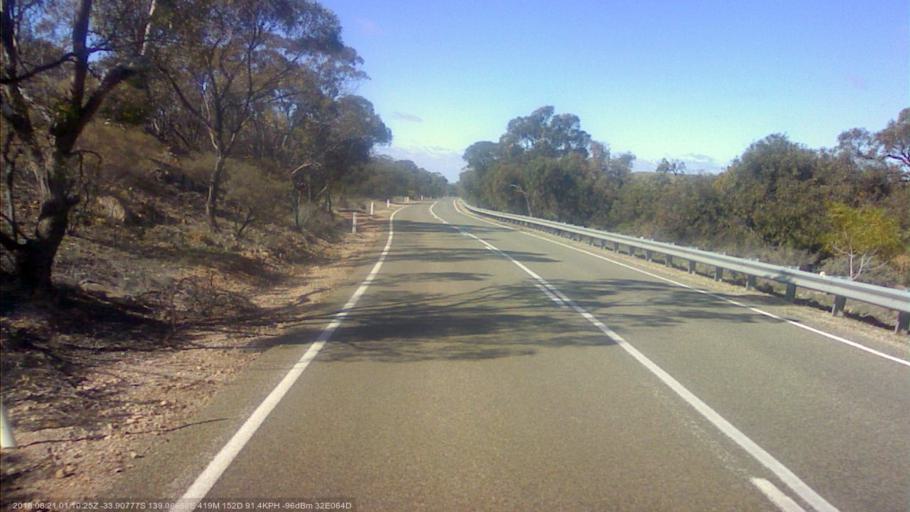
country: AU
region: South Australia
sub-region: Light
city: Kapunda
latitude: -33.9078
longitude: 139.0866
